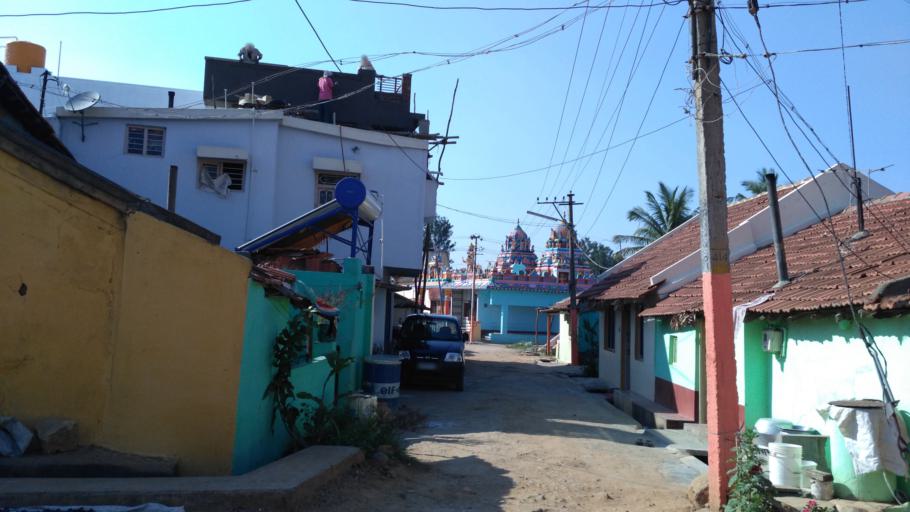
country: IN
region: Karnataka
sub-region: Hassan
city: Hassan
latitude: 12.9999
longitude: 76.1257
